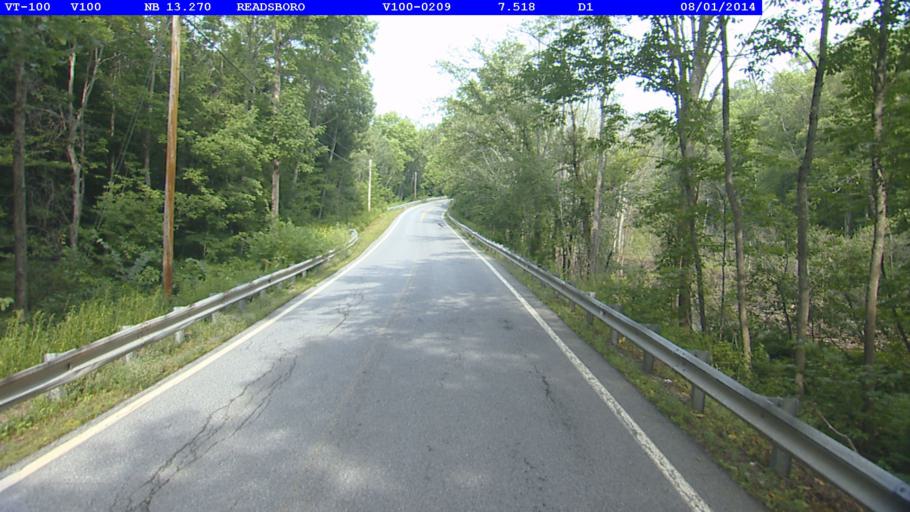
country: US
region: Massachusetts
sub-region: Franklin County
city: Charlemont
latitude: 42.7701
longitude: -72.9386
